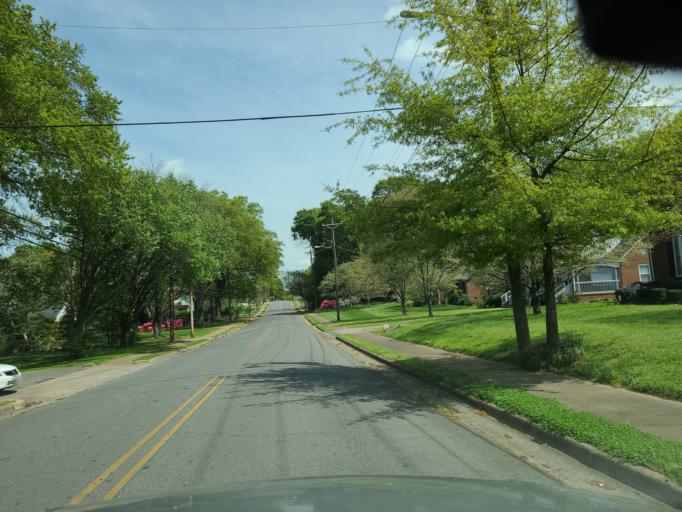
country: US
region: North Carolina
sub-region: Cleveland County
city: Shelby
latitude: 35.2937
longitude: -81.5496
